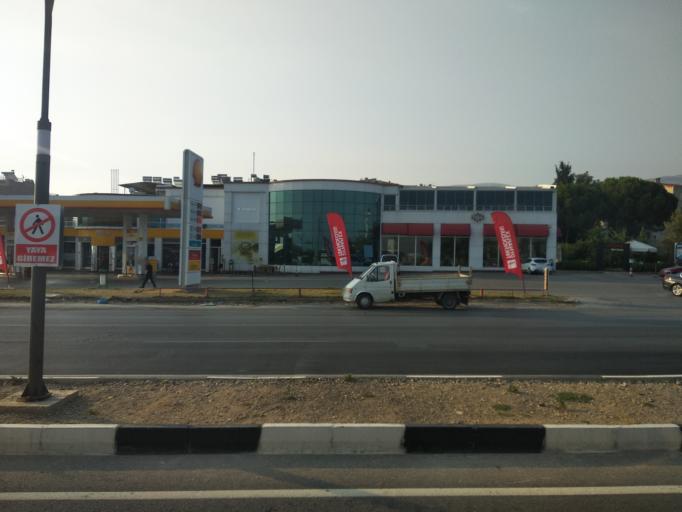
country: TR
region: Manisa
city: Salihli
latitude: 38.4872
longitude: 28.1313
